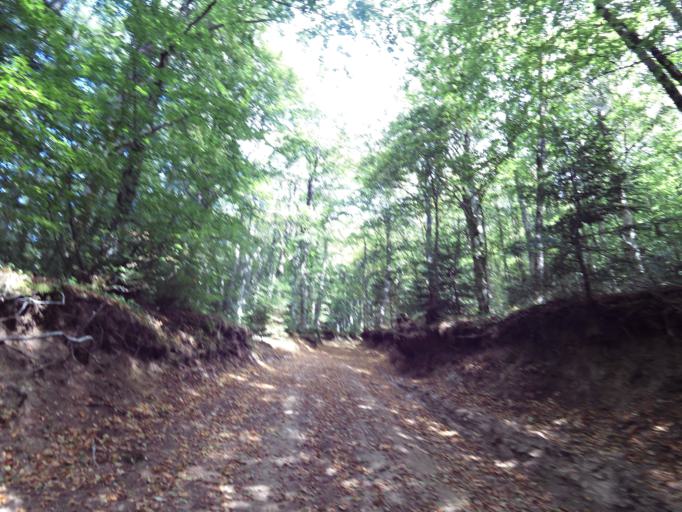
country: IT
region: Calabria
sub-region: Provincia di Vibo-Valentia
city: Mongiana
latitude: 38.5234
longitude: 16.3458
